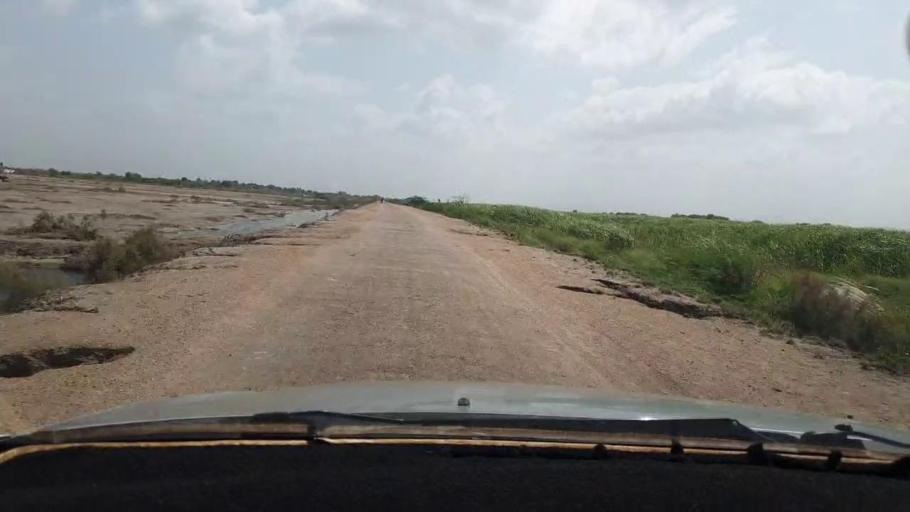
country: PK
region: Sindh
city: Tando Bago
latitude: 24.7206
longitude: 69.1836
